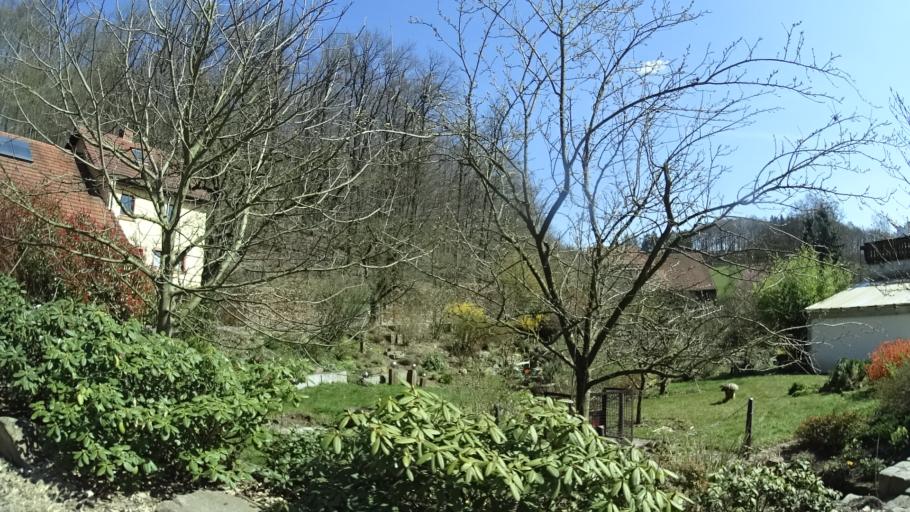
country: DE
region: Hesse
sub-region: Regierungsbezirk Darmstadt
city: Wald-Michelbach
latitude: 49.5936
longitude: 8.8142
